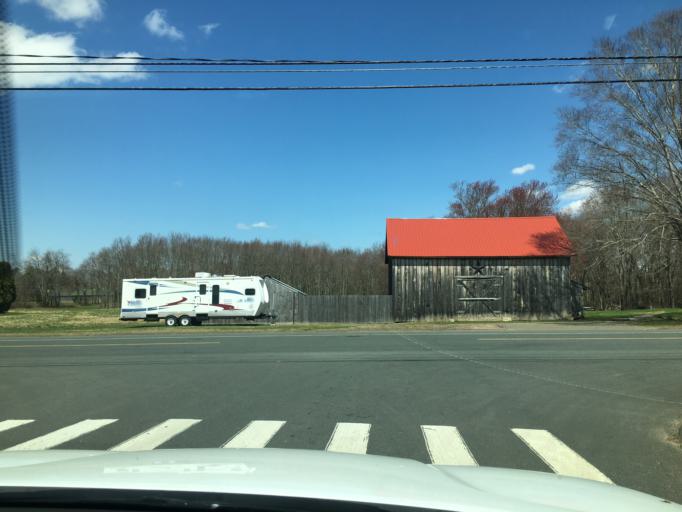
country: US
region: Connecticut
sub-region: Hartford County
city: Hazardville
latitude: 42.0026
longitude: -72.5304
